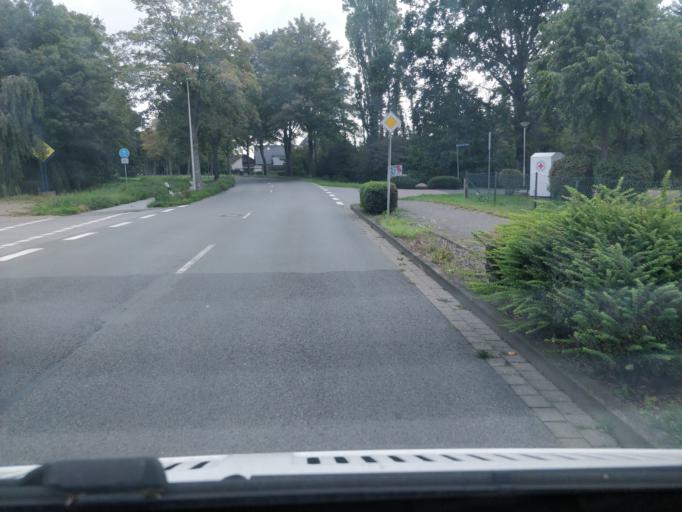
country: DE
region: North Rhine-Westphalia
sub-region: Regierungsbezirk Dusseldorf
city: Emmerich
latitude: 51.8383
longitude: 6.2669
